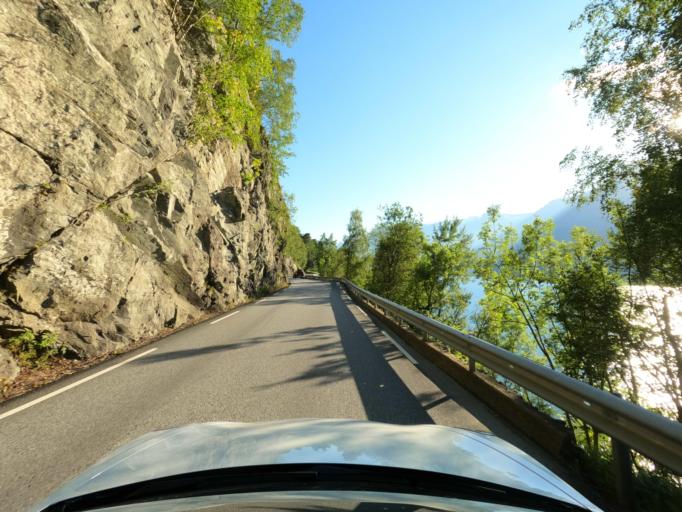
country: NO
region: Hordaland
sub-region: Ullensvang
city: Kinsarvik
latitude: 60.2838
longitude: 6.6232
